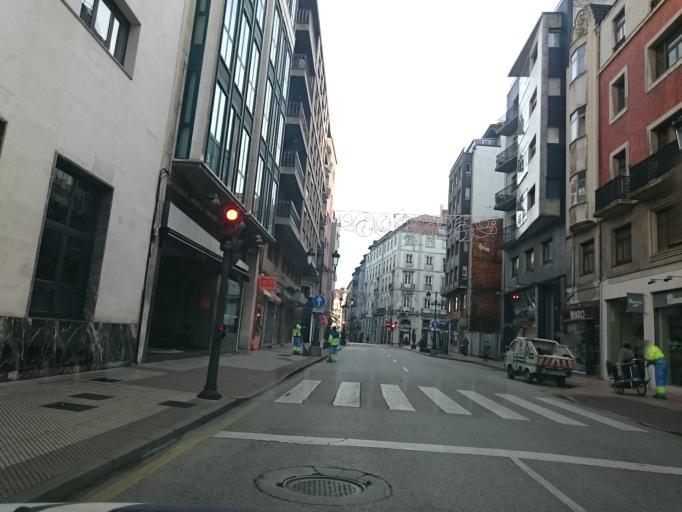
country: ES
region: Asturias
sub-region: Province of Asturias
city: Oviedo
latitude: 43.3636
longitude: -5.8418
